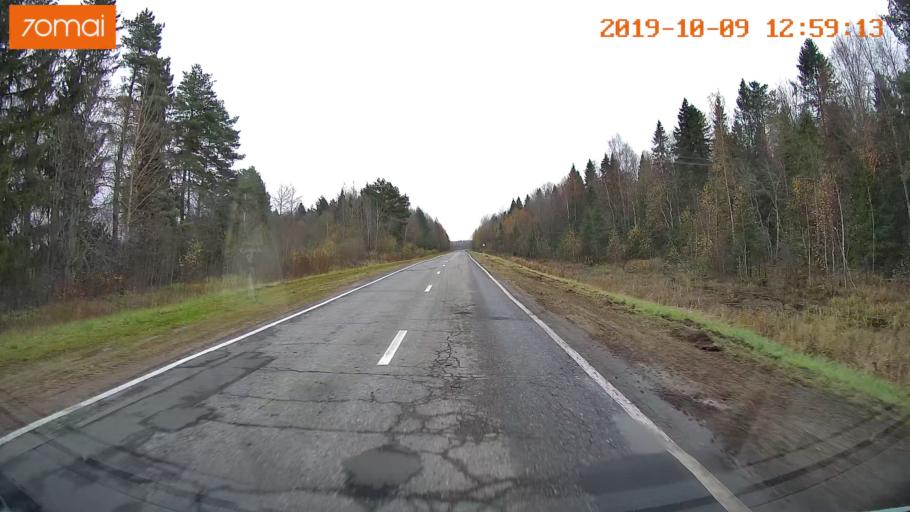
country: RU
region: Jaroslavl
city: Prechistoye
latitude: 58.3844
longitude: 40.4602
